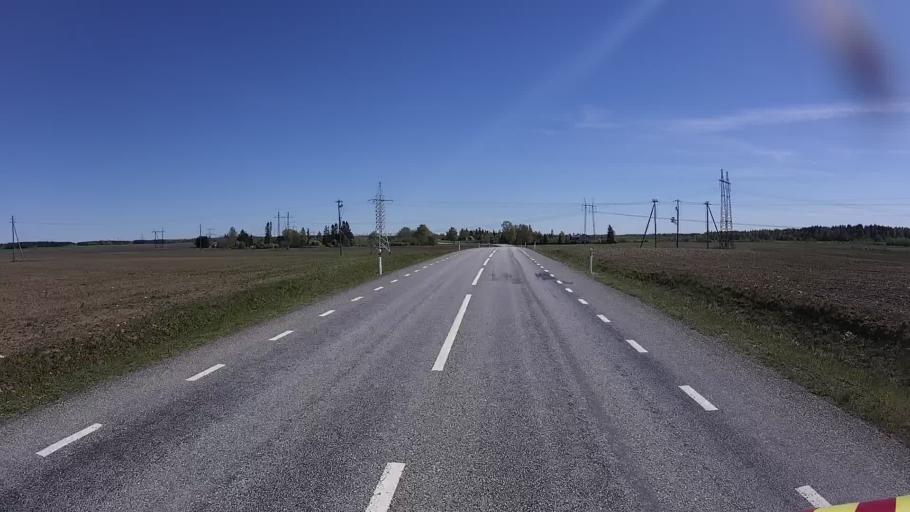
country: EE
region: Laeaene-Virumaa
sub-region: Tapa vald
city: Tapa
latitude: 59.2372
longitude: 25.7025
